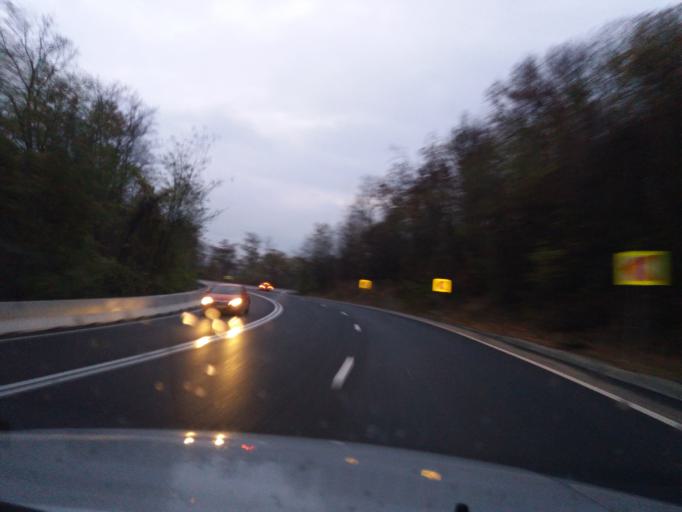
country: RO
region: Hunedoara
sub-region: Comuna Santamaria-Orlea
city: Santamaria-Orlea
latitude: 45.6164
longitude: 22.9844
